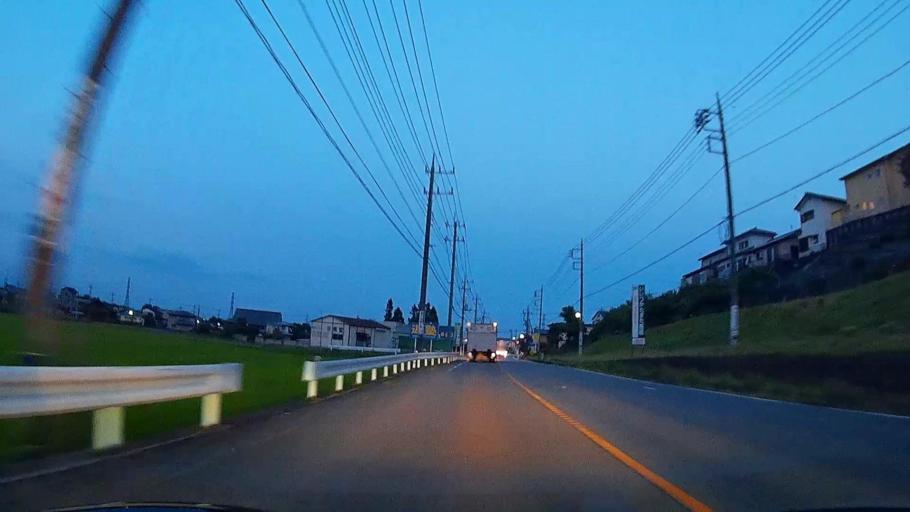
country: JP
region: Gunma
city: Takasaki
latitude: 36.3465
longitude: 138.9564
